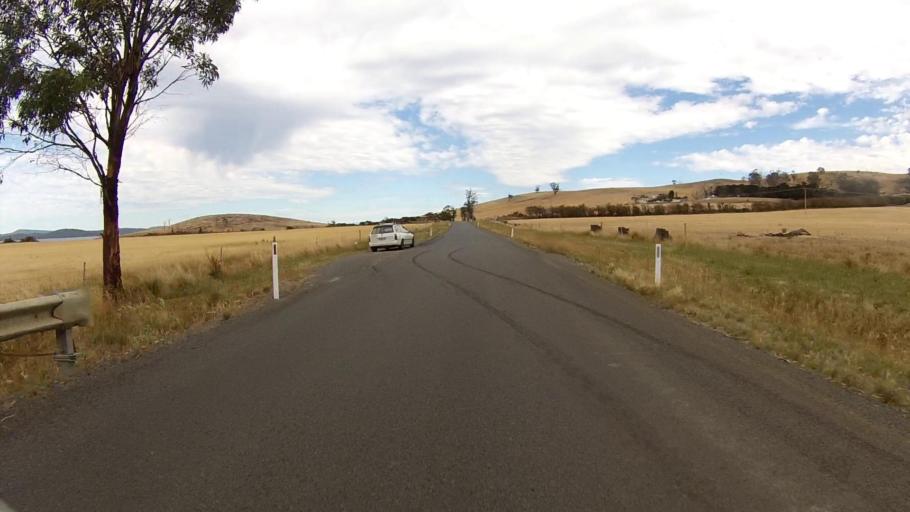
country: AU
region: Tasmania
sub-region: Sorell
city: Sorell
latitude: -42.8943
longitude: 147.7779
